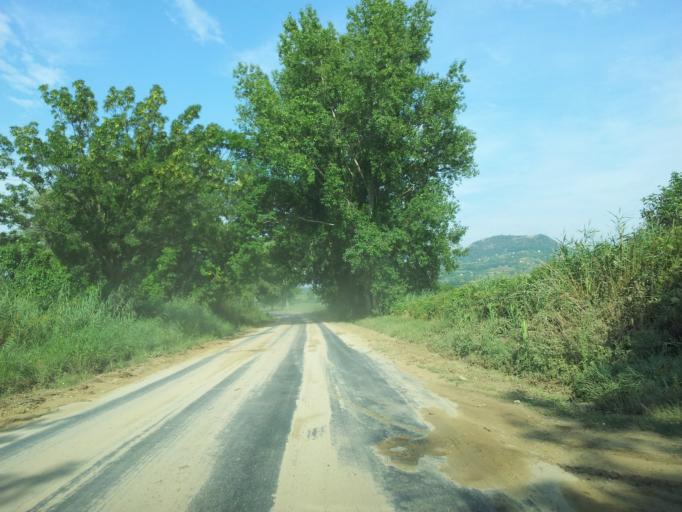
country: HU
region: Veszprem
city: Badacsonytomaj
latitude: 46.8545
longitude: 17.5332
